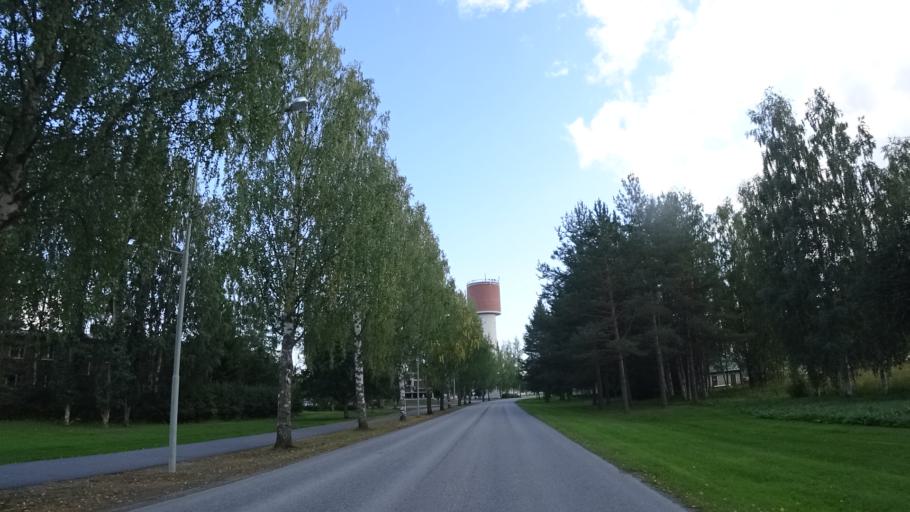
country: FI
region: North Karelia
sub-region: Pielisen Karjala
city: Lieksa
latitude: 63.3236
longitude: 30.0226
